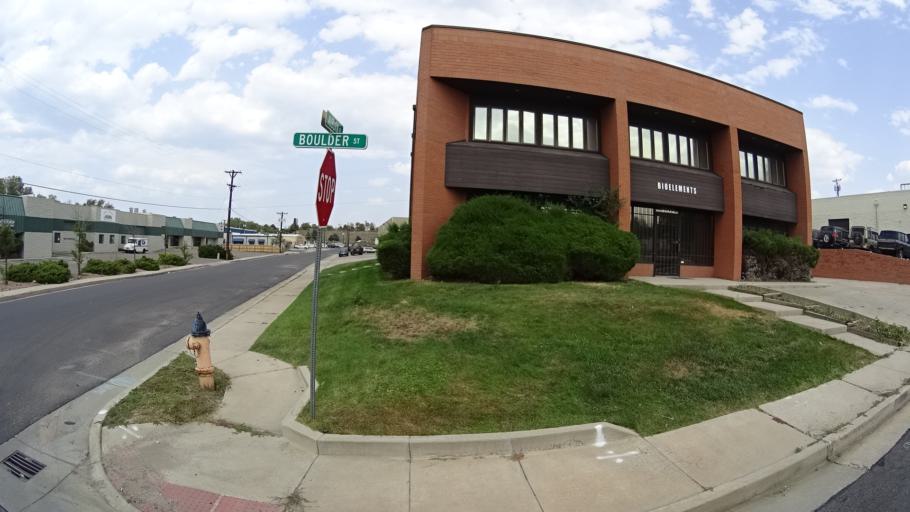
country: US
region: Colorado
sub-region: El Paso County
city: Colorado Springs
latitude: 38.8373
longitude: -104.7628
